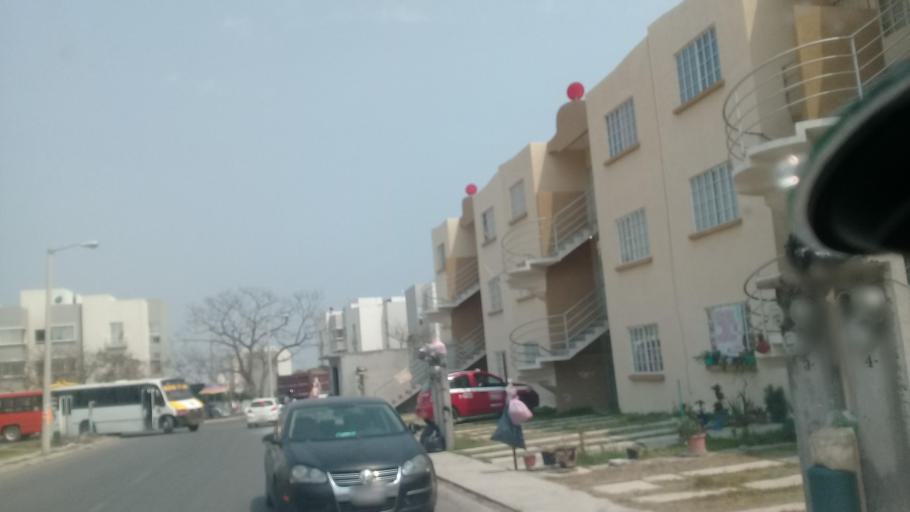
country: MX
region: Veracruz
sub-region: Veracruz
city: Lomas de Rio Medio Cuatro
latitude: 19.1819
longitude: -96.2102
